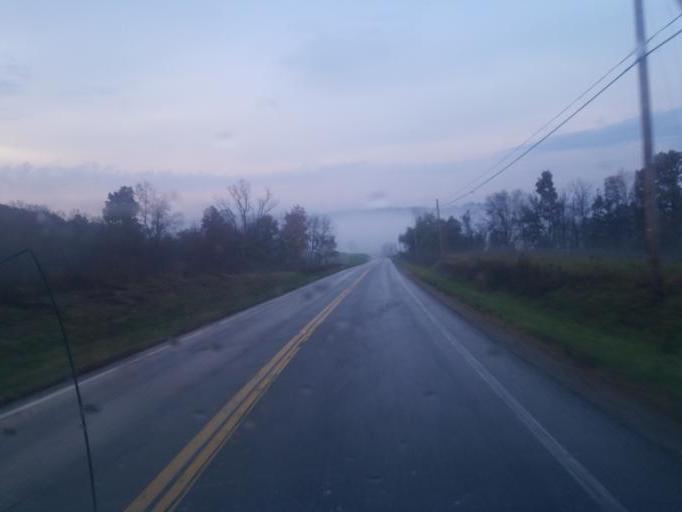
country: US
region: Ohio
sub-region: Morgan County
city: McConnelsville
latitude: 39.5115
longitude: -81.8525
